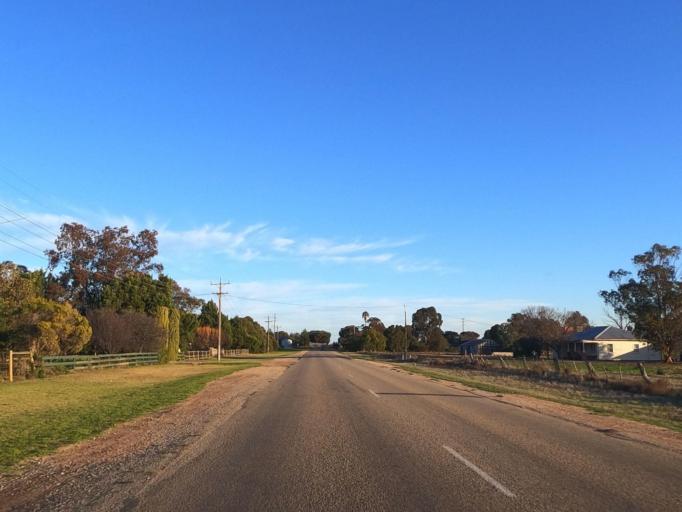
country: AU
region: Victoria
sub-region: Swan Hill
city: Swan Hill
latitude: -35.3582
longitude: 143.5521
